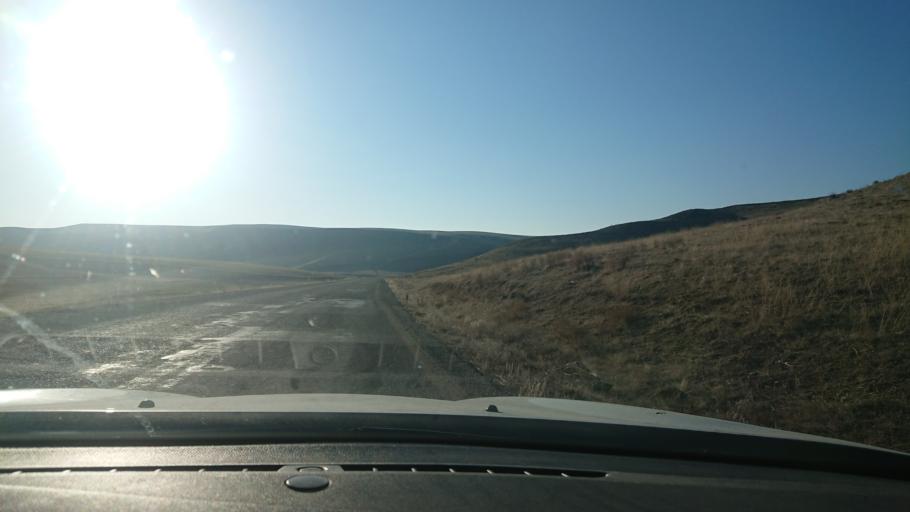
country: TR
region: Aksaray
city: Acipinar
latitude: 38.7112
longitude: 33.7689
